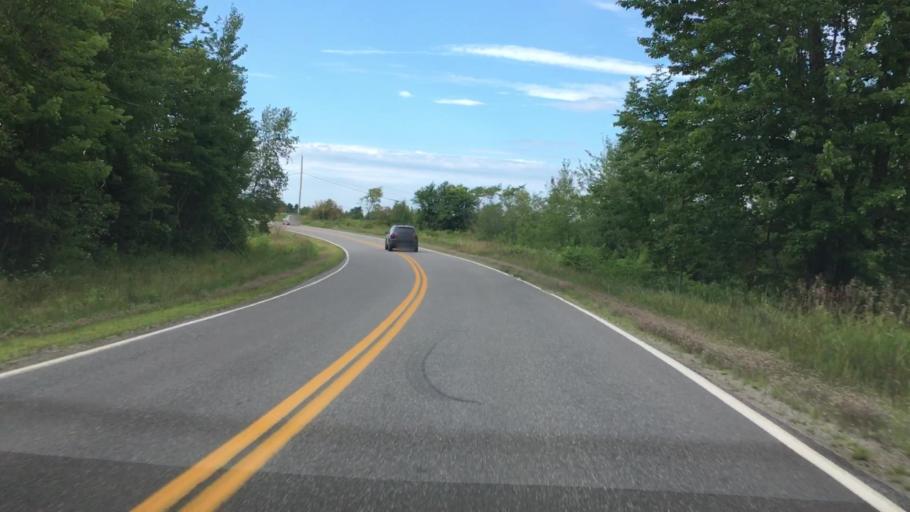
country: US
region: Maine
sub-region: Waldo County
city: Belfast
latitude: 44.3745
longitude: -69.0315
